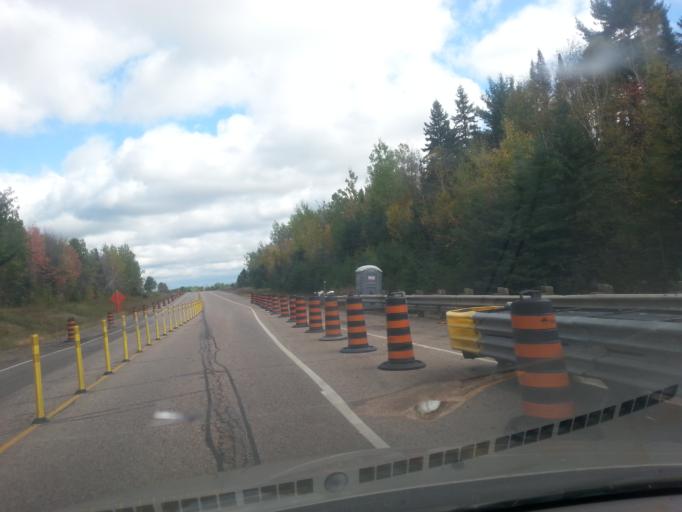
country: CA
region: Ontario
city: Pembroke
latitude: 45.7991
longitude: -77.1366
